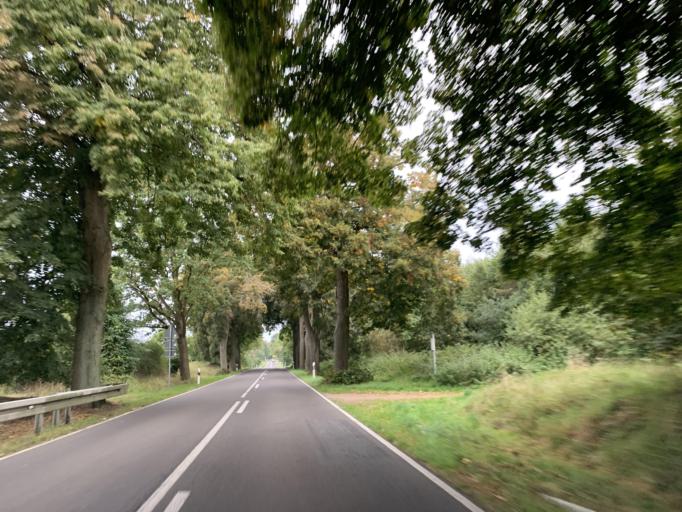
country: DE
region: Mecklenburg-Vorpommern
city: Loitz
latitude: 53.3399
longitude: 13.4818
